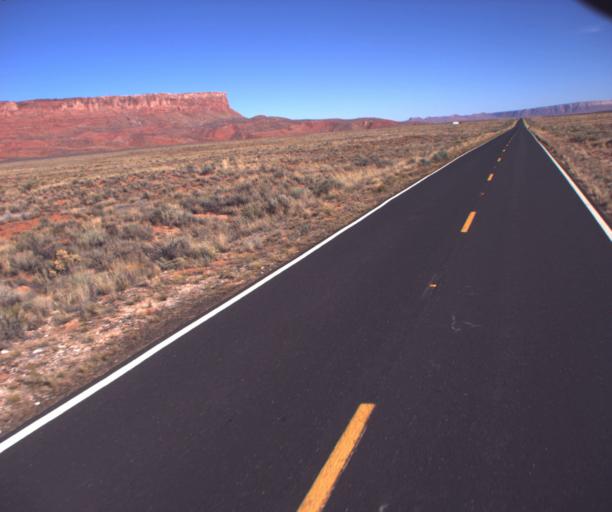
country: US
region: Arizona
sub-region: Coconino County
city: Page
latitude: 36.6987
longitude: -111.9203
